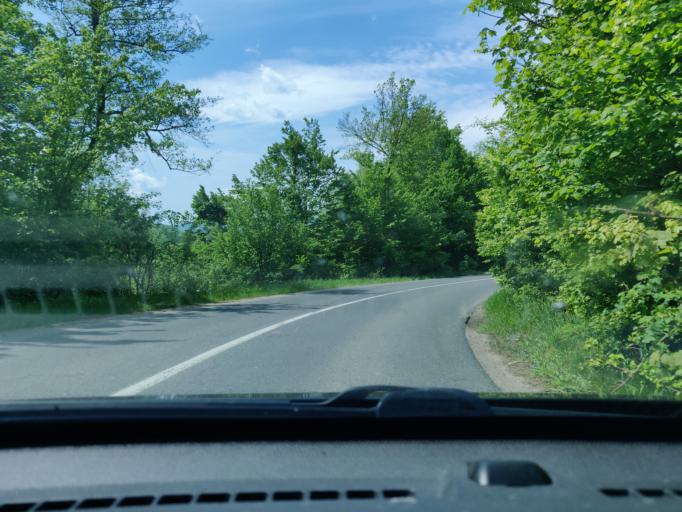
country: RO
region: Vrancea
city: Dragosloveni
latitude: 46.0337
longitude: 26.6966
